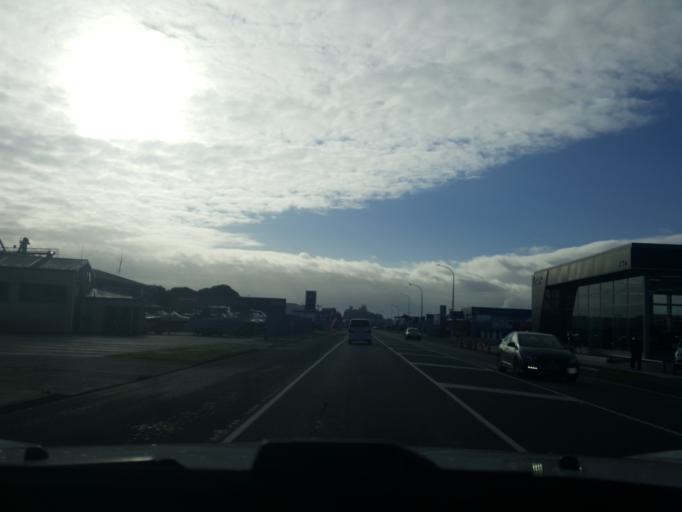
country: NZ
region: Waikato
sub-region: Waipa District
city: Cambridge
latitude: -37.6611
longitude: 175.5192
